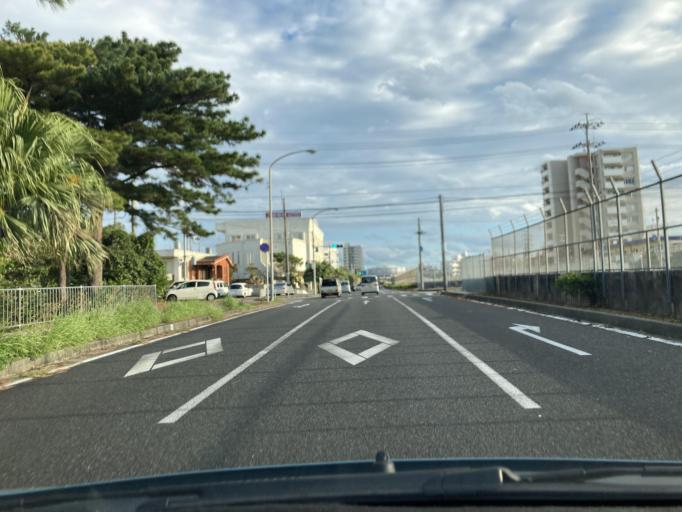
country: JP
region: Okinawa
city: Okinawa
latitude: 26.3272
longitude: 127.7864
